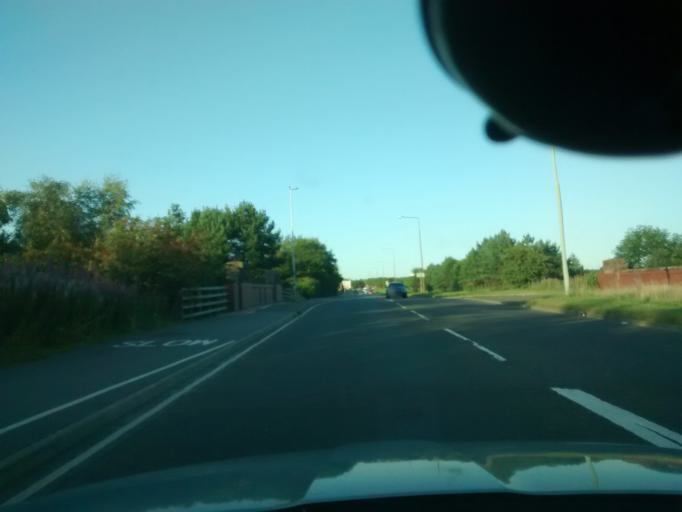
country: GB
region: Scotland
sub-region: West Lothian
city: Bathgate
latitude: 55.8931
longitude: -3.6110
